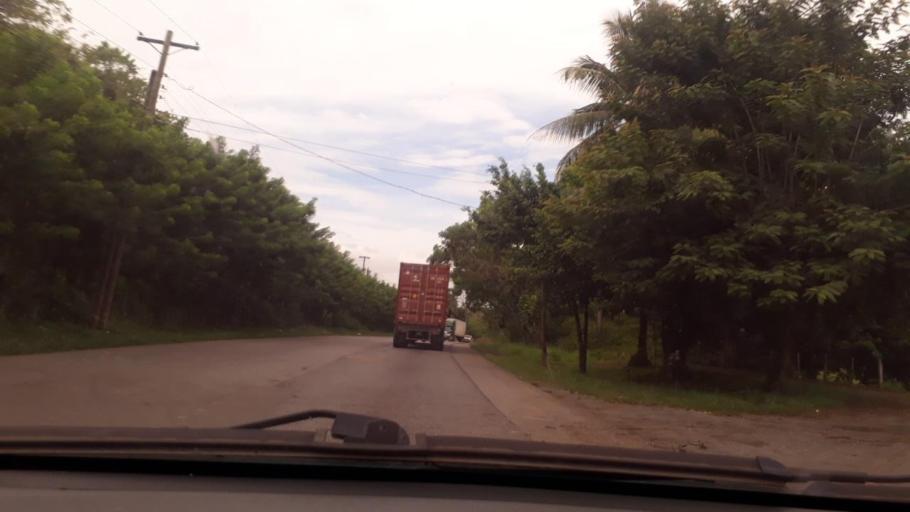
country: GT
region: Izabal
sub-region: Municipio de Puerto Barrios
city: Puerto Barrios
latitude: 15.5810
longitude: -88.6102
